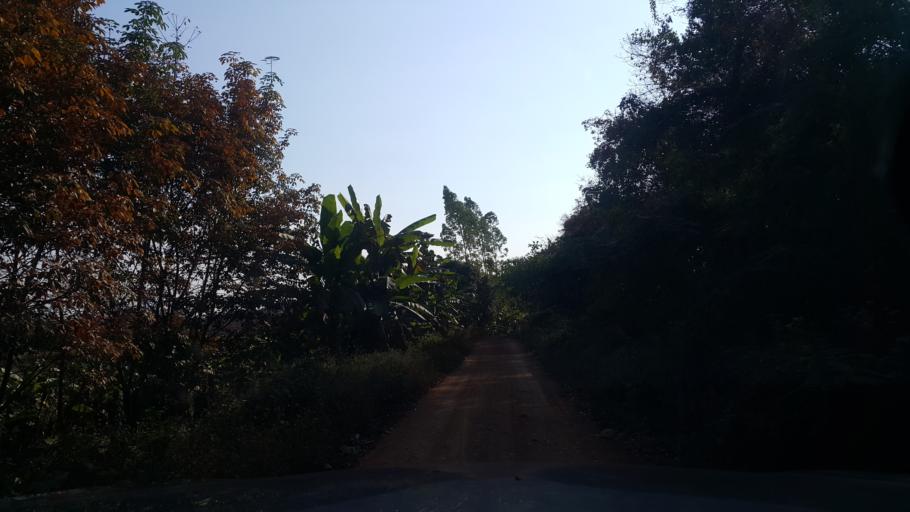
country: TH
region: Loei
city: Chiang Khan
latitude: 17.8282
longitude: 101.6125
